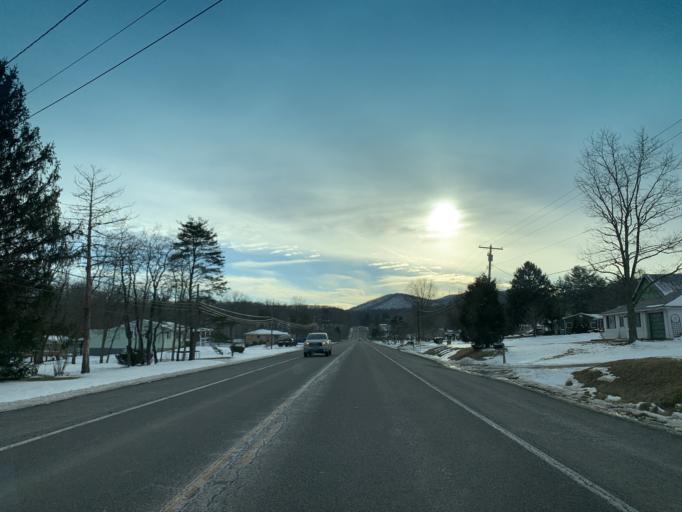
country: US
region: West Virginia
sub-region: Mineral County
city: Keyser
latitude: 39.4651
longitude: -78.9659
